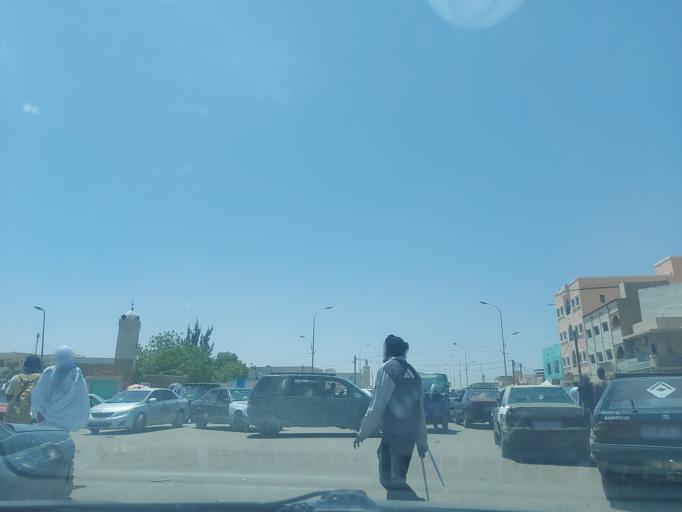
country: MR
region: Nouakchott
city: Nouakchott
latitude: 18.0823
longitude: -15.9814
